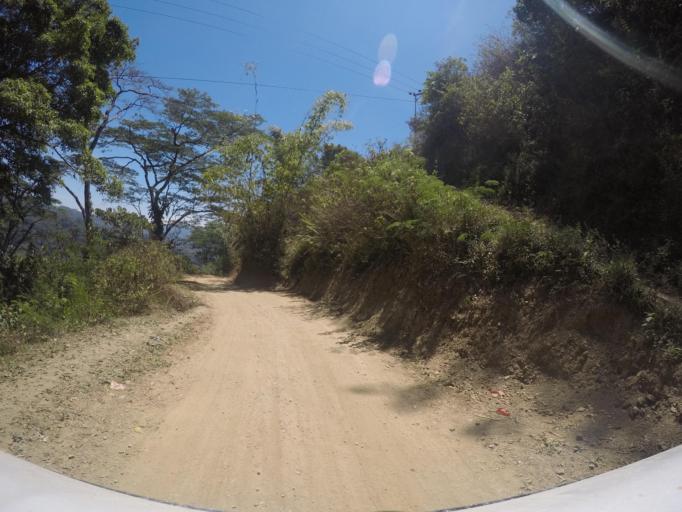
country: TL
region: Ermera
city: Gleno
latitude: -8.7426
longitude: 125.4037
